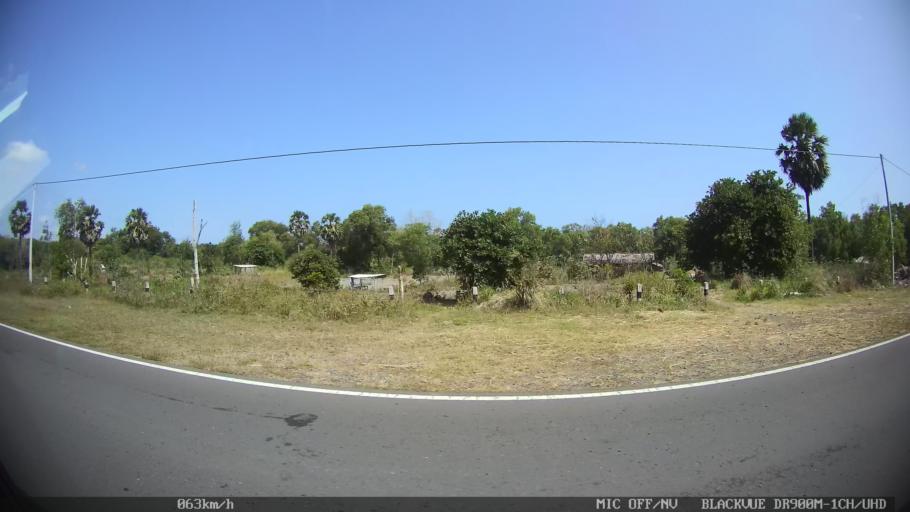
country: ID
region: Daerah Istimewa Yogyakarta
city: Bambanglipuro
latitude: -8.0109
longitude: 110.3058
